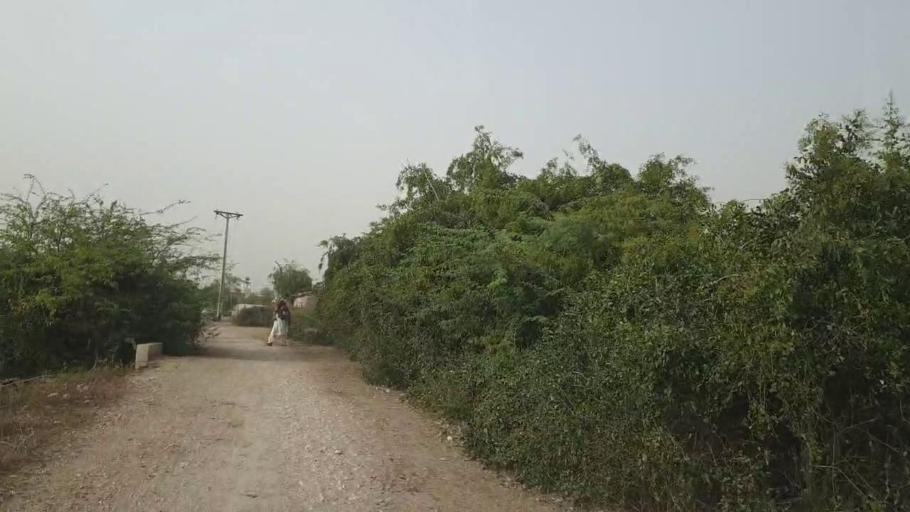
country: PK
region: Sindh
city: Kunri
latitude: 25.0695
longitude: 69.4879
